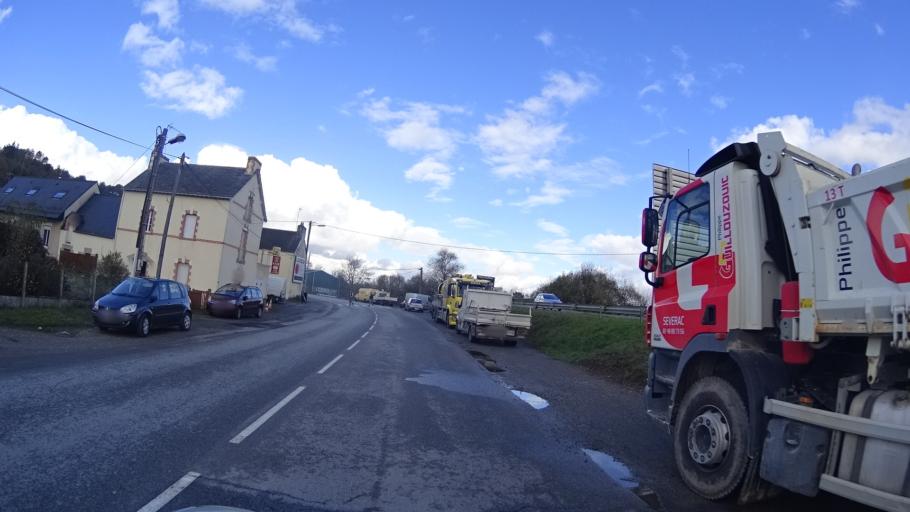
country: FR
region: Brittany
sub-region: Departement du Morbihan
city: Saint-Jean-la-Poterie
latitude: 47.6325
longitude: -2.1020
